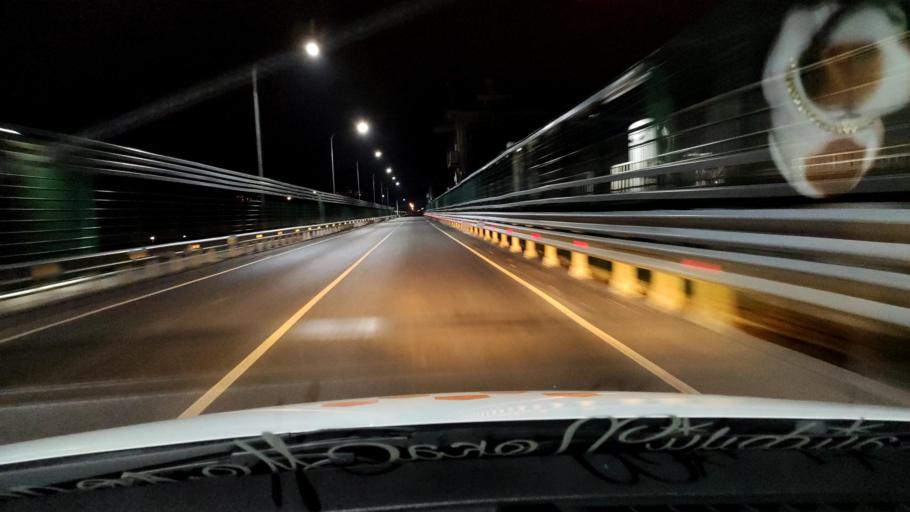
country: RU
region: Voronezj
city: Shilovo
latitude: 51.5377
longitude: 39.1388
